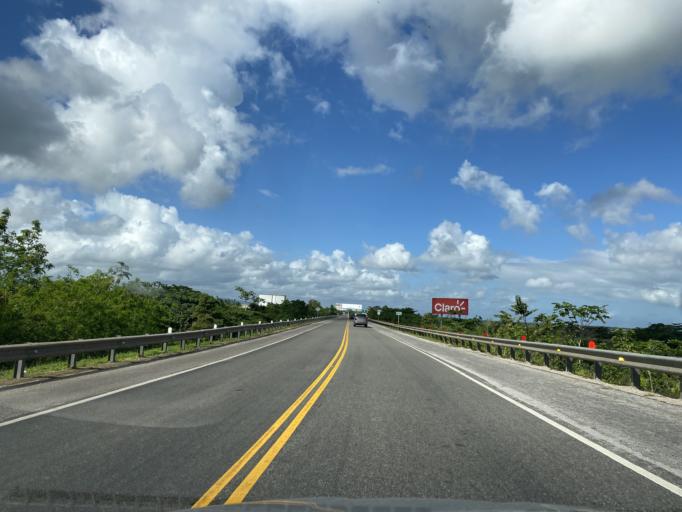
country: DO
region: Duarte
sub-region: Villa Riva
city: Agua Santa del Yuna
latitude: 19.1118
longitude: -69.8337
